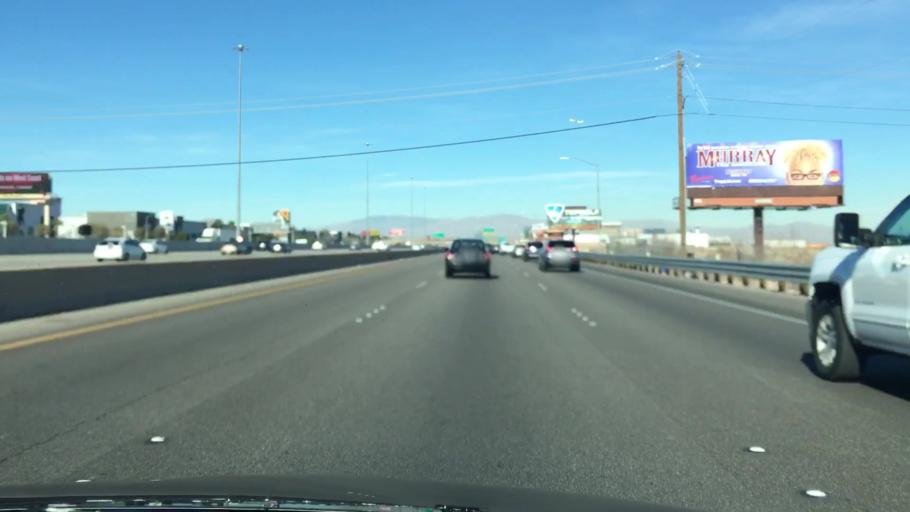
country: US
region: Nevada
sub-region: Clark County
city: Paradise
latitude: 36.0495
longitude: -115.1805
